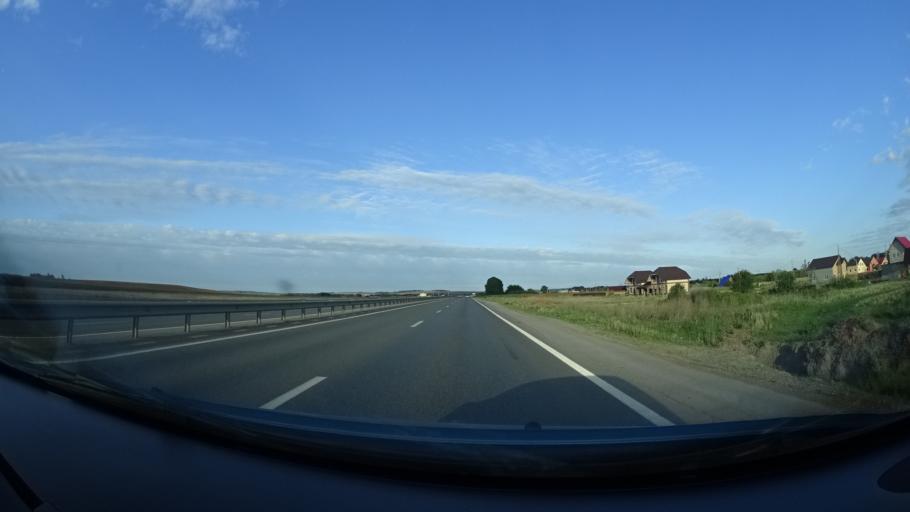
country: RU
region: Perm
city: Kultayevo
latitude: 57.8934
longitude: 55.9554
